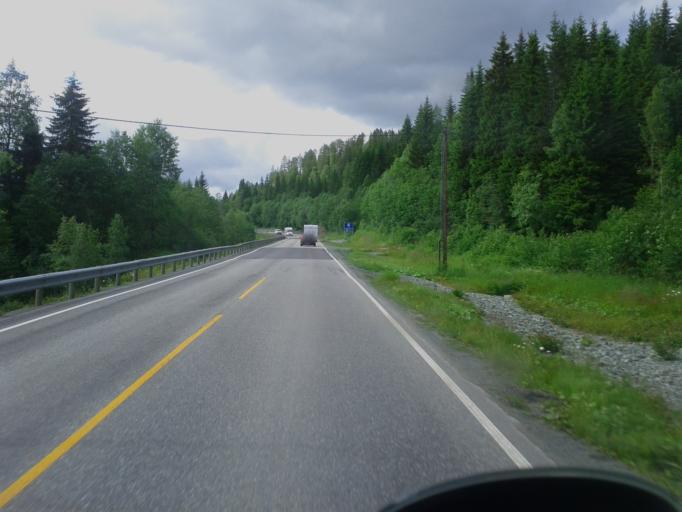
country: NO
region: Nord-Trondelag
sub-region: Grong
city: Grong
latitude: 64.5409
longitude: 12.4490
